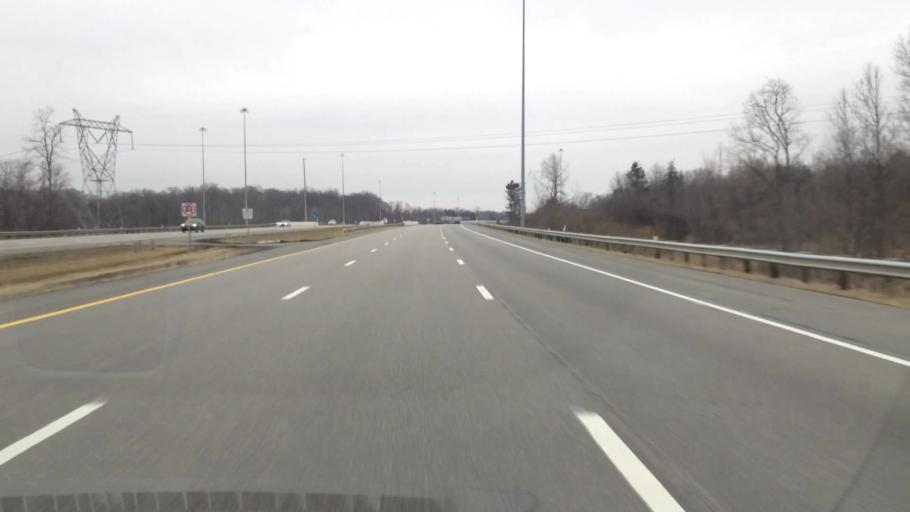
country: US
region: Ohio
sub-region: Medina County
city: Medina
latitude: 41.1642
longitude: -81.7856
